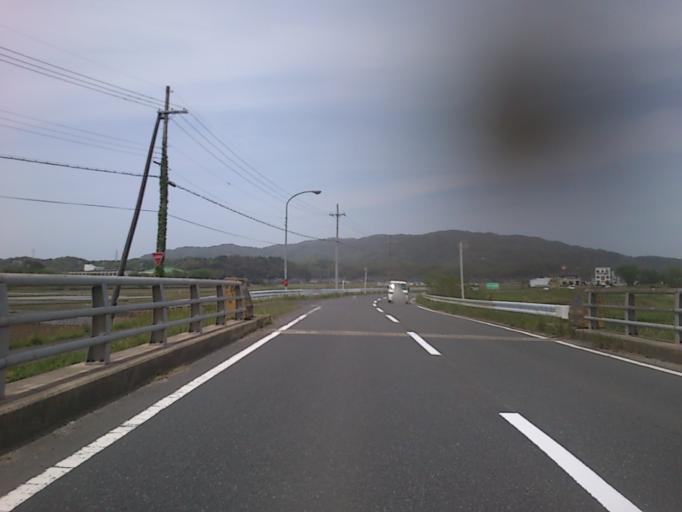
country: JP
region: Kyoto
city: Miyazu
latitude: 35.6642
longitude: 135.0861
